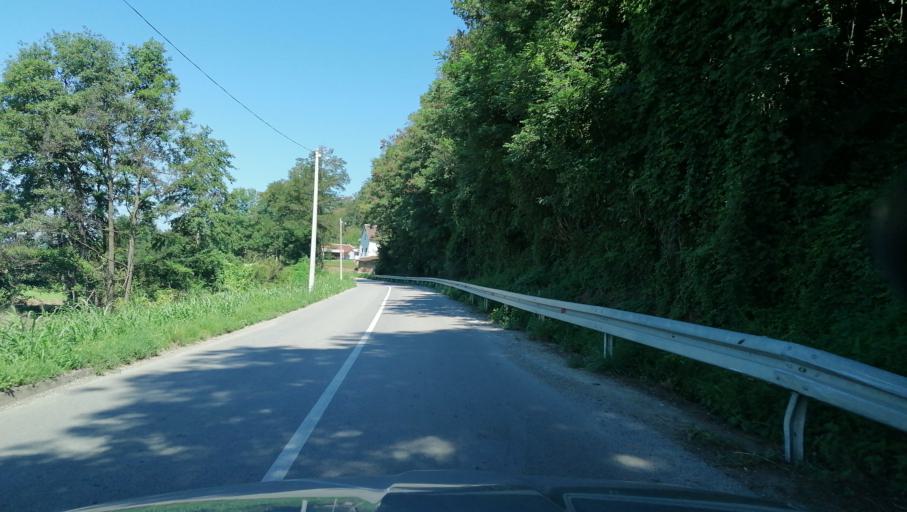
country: RS
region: Central Serbia
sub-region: Raski Okrug
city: Vrnjacka Banja
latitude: 43.6912
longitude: 20.8664
